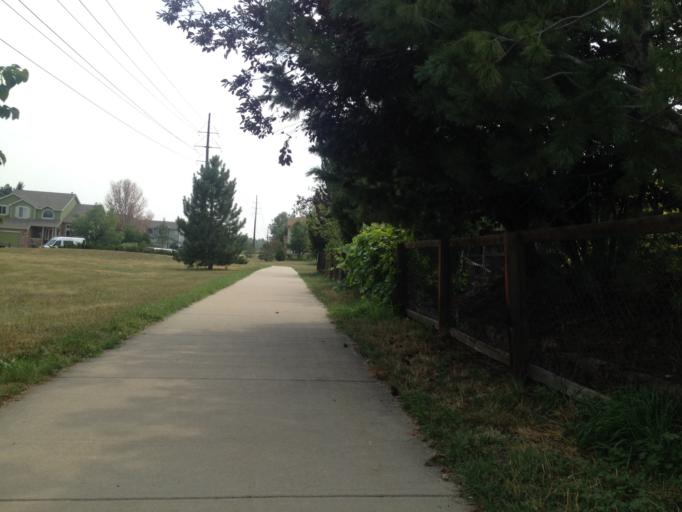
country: US
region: Colorado
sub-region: Boulder County
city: Superior
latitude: 39.9632
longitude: -105.1565
